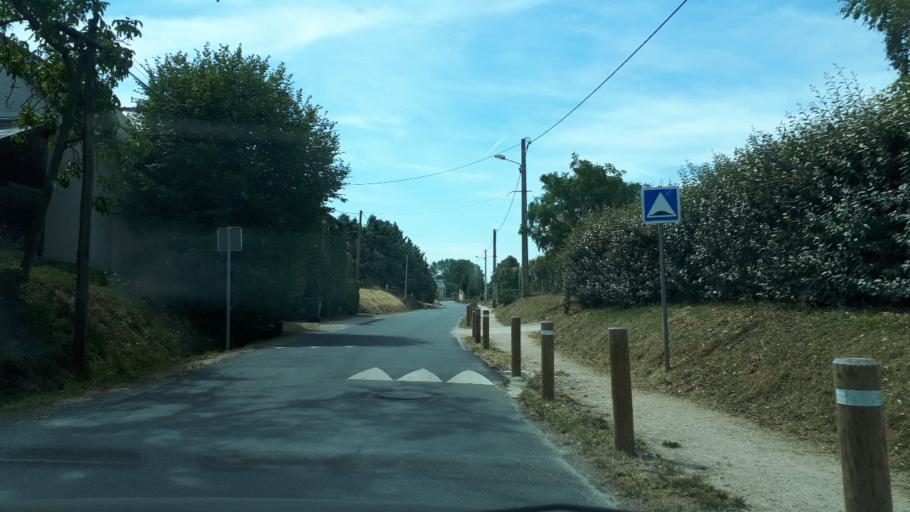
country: FR
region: Centre
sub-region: Departement du Loir-et-Cher
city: Contres
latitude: 47.3939
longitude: 1.3780
